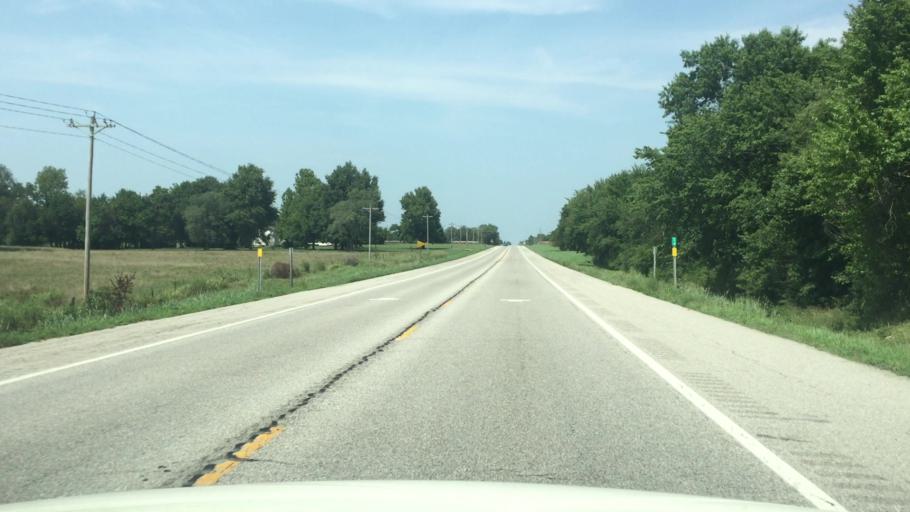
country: US
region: Missouri
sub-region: Jasper County
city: Carl Junction
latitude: 37.2459
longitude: -94.7050
